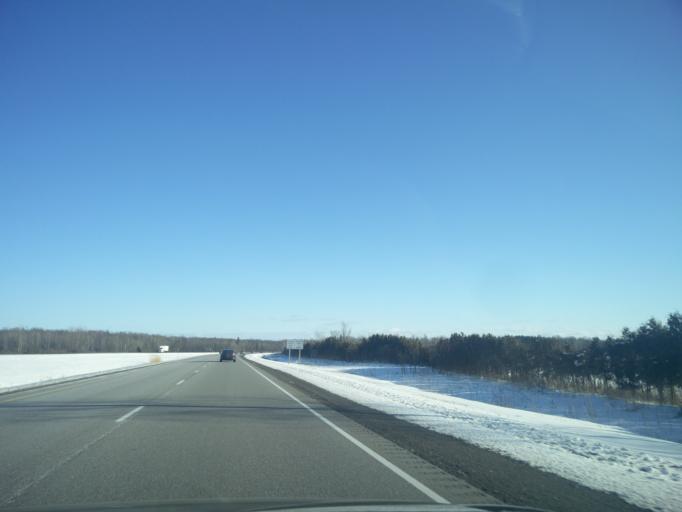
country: CA
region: Ontario
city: Prescott
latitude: 44.9422
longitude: -75.5803
